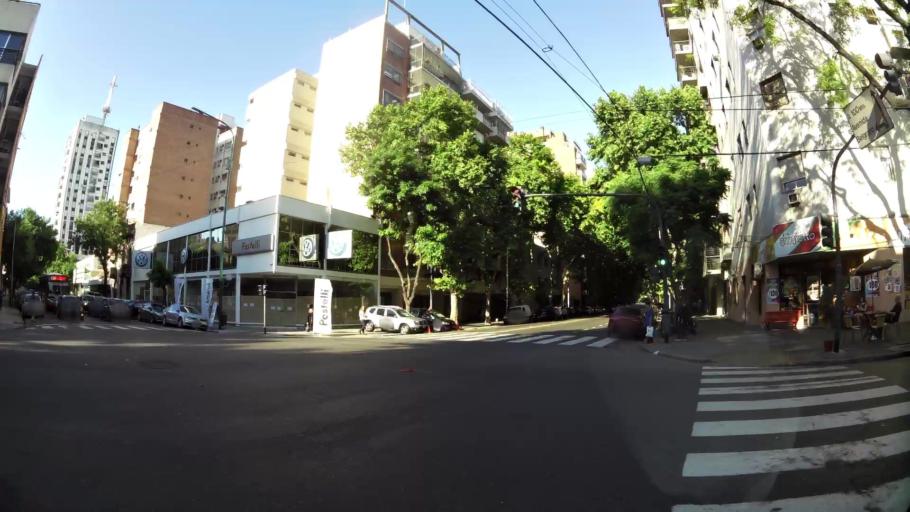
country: AR
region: Buenos Aires F.D.
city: Buenos Aires
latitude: -34.6148
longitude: -58.4204
